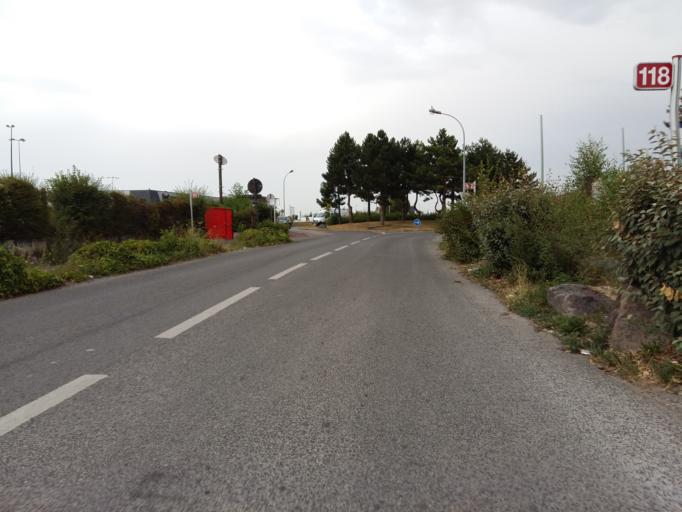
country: FR
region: Picardie
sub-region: Departement de la Somme
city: Camon
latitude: 49.8990
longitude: 2.3404
